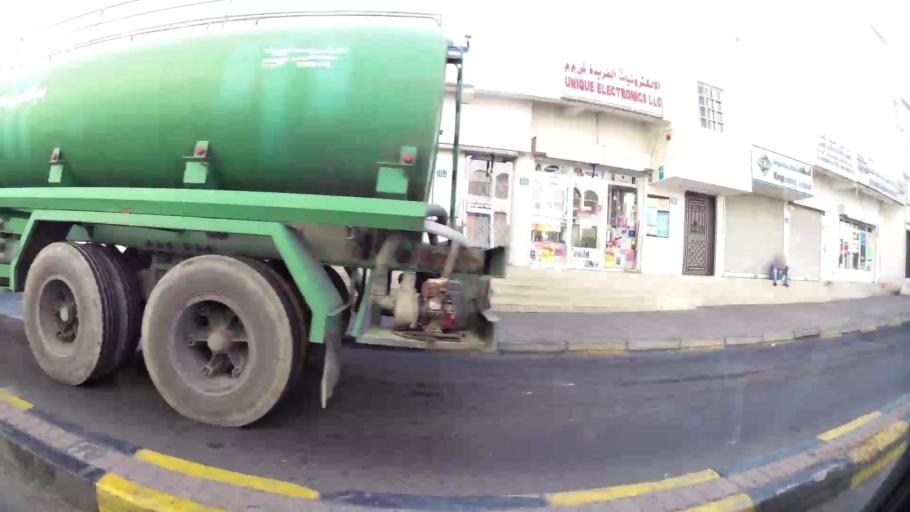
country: OM
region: Muhafazat Masqat
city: Muscat
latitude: 23.5849
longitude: 58.5456
